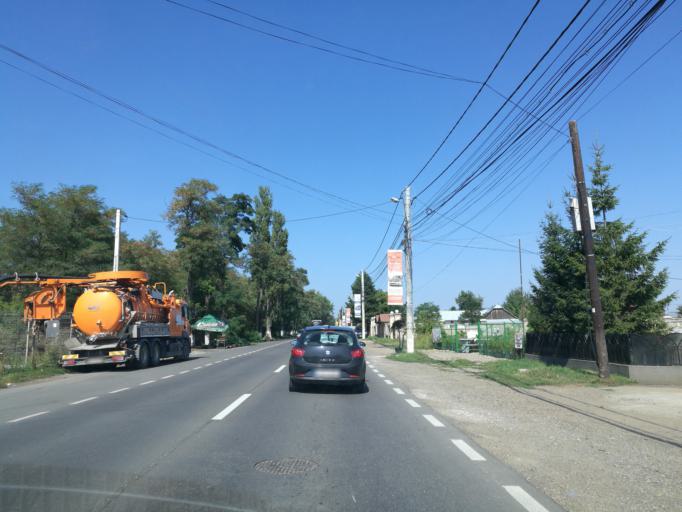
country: RO
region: Suceava
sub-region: Municipiul Suceava
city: Radauti
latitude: 47.8311
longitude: 25.9344
